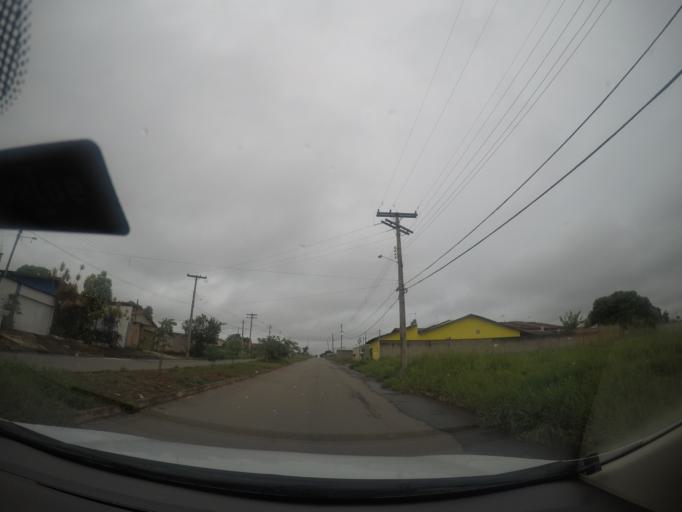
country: BR
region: Goias
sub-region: Aparecida De Goiania
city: Aparecida de Goiania
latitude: -16.7570
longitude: -49.3177
